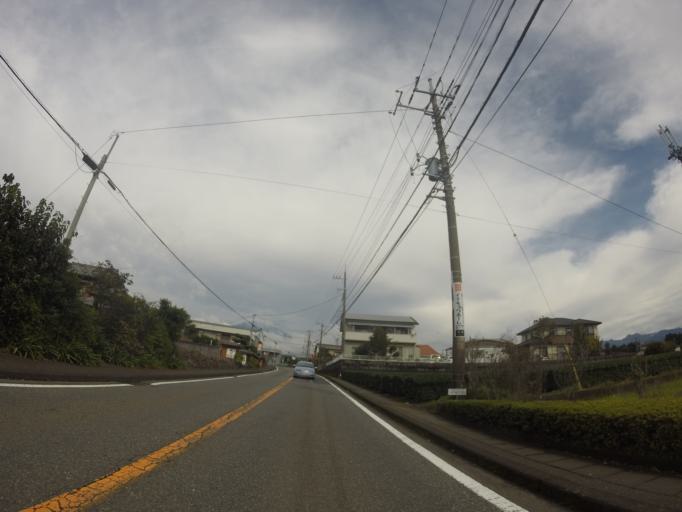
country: JP
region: Shizuoka
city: Fuji
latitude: 35.2079
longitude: 138.6851
